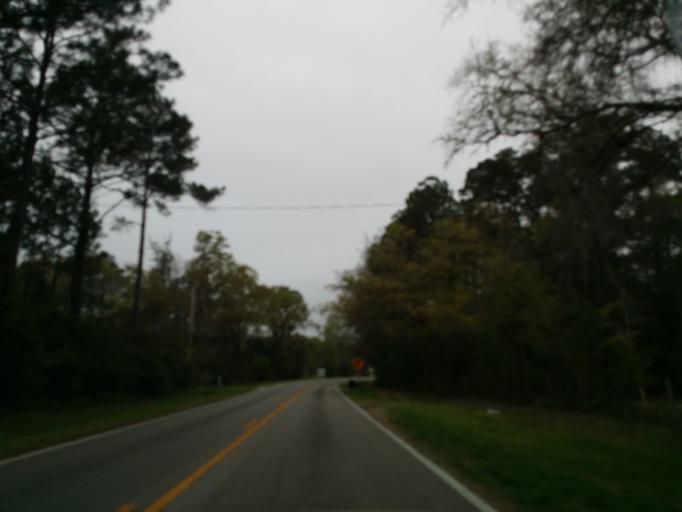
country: US
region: Florida
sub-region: Leon County
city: Woodville
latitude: 30.3214
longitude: -84.2634
